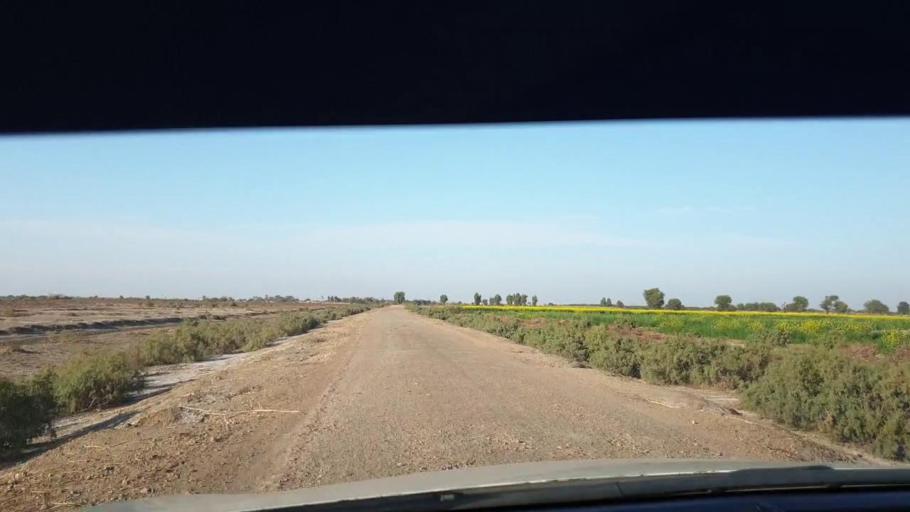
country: PK
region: Sindh
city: Berani
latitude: 25.8145
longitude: 68.9100
